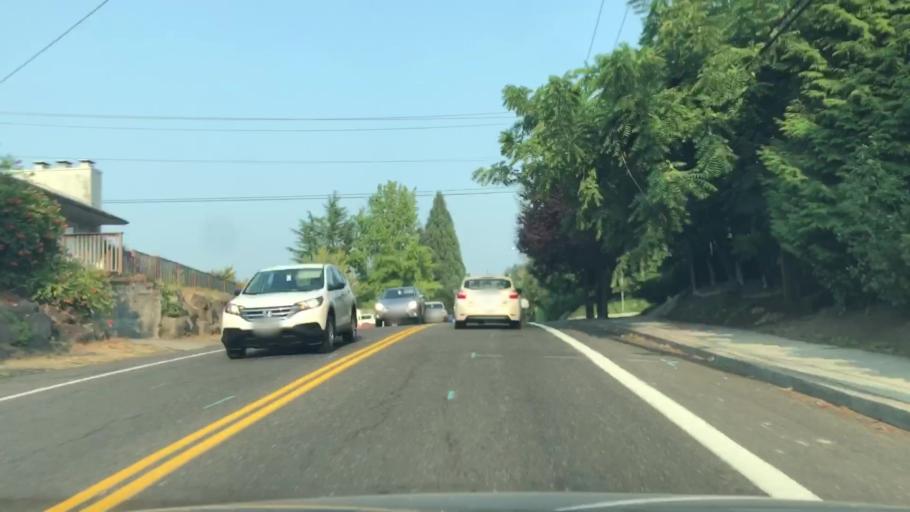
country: US
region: Oregon
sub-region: Washington County
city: Garden Home-Whitford
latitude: 45.4761
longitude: -122.7182
